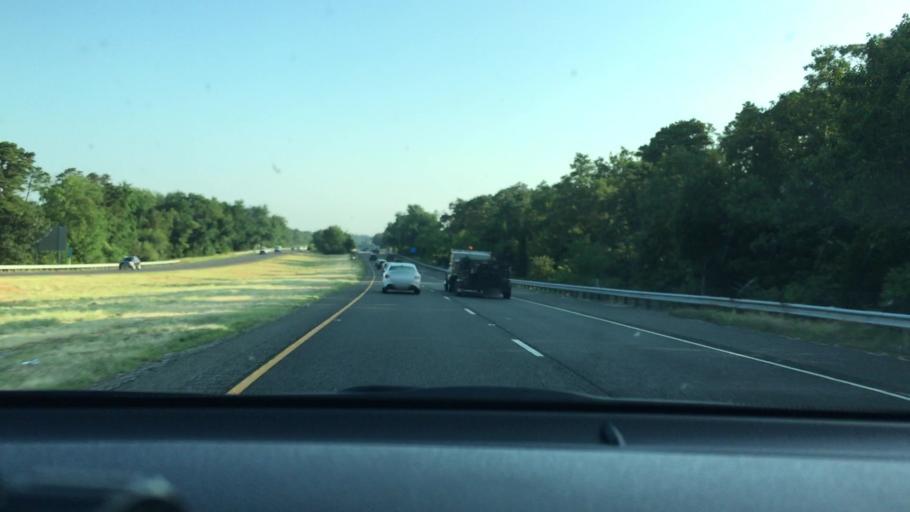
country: US
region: New Jersey
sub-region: Cumberland County
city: Vineland
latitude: 39.5064
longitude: -75.0692
